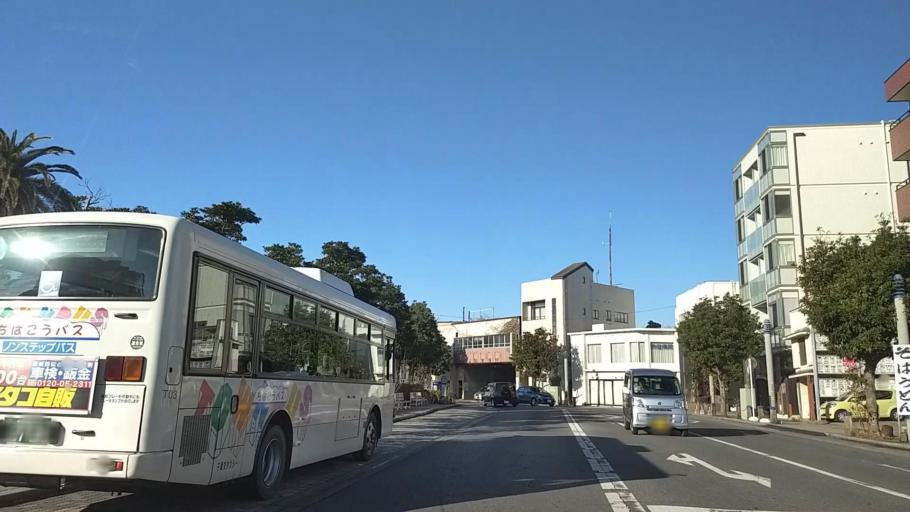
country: JP
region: Chiba
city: Hasaki
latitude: 35.7302
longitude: 140.8274
